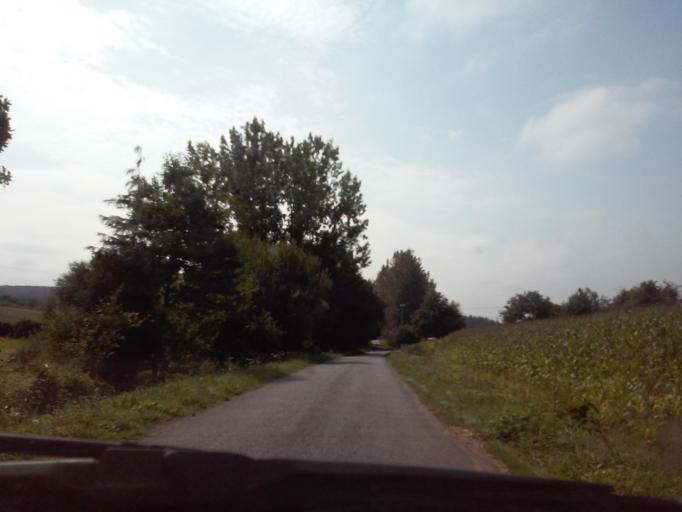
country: FR
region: Brittany
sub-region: Departement du Morbihan
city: Ploermel
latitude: 47.8988
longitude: -2.4090
